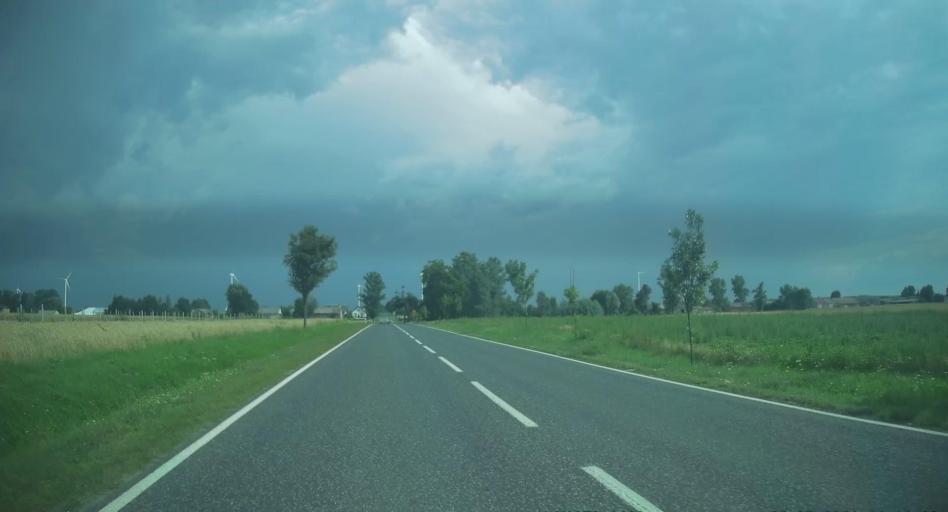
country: PL
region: Lodz Voivodeship
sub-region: Powiat brzezinski
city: Jezow
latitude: 51.8004
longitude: 20.0224
